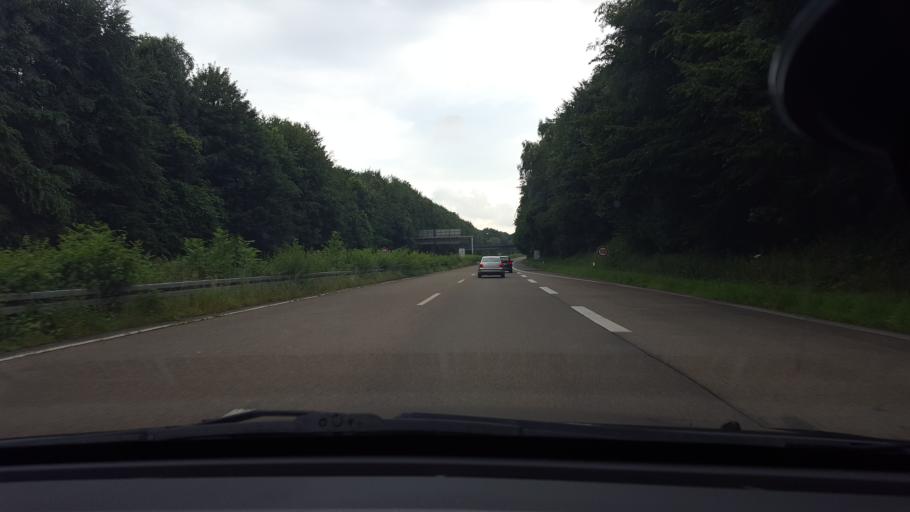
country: DE
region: North Rhine-Westphalia
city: Herten
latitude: 51.6174
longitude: 7.1619
